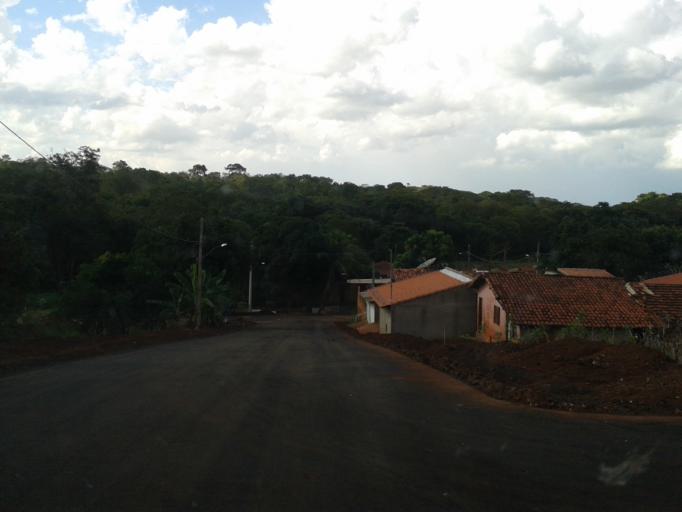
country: BR
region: Minas Gerais
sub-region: Capinopolis
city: Capinopolis
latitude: -18.6824
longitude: -49.5822
